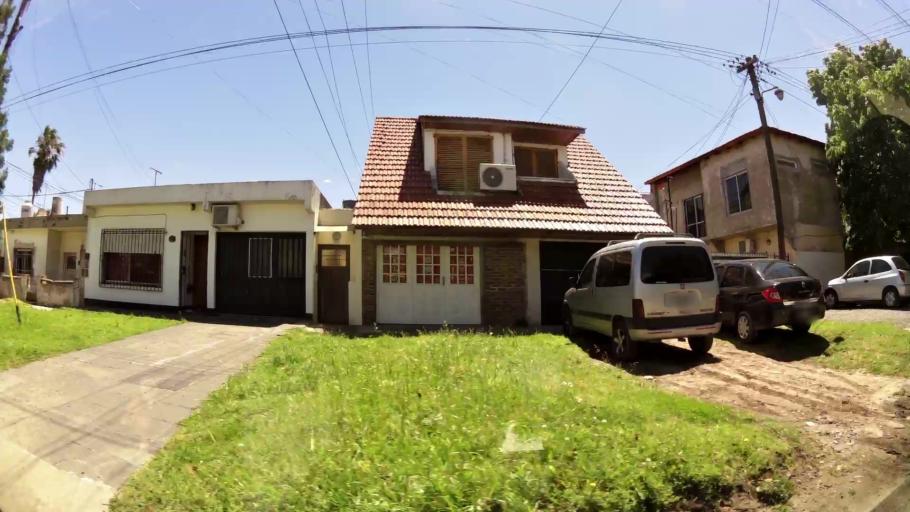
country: AR
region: Buenos Aires
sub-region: Partido de Quilmes
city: Quilmes
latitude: -34.7365
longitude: -58.2872
